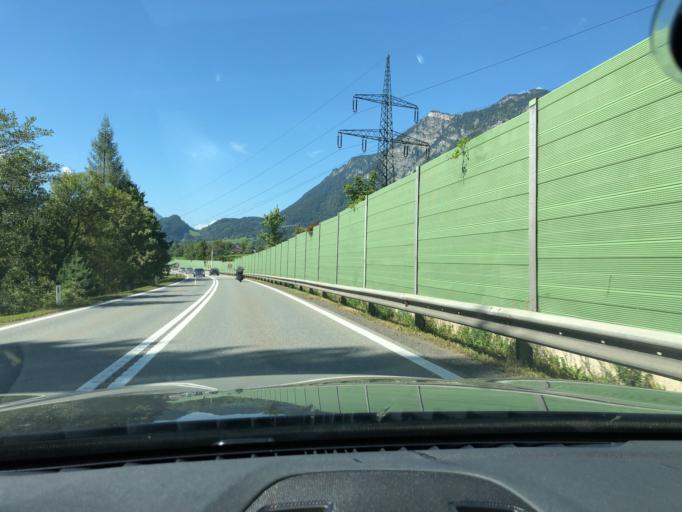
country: AT
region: Vorarlberg
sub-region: Politischer Bezirk Bludenz
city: Innerbraz
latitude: 47.1433
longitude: 9.9177
